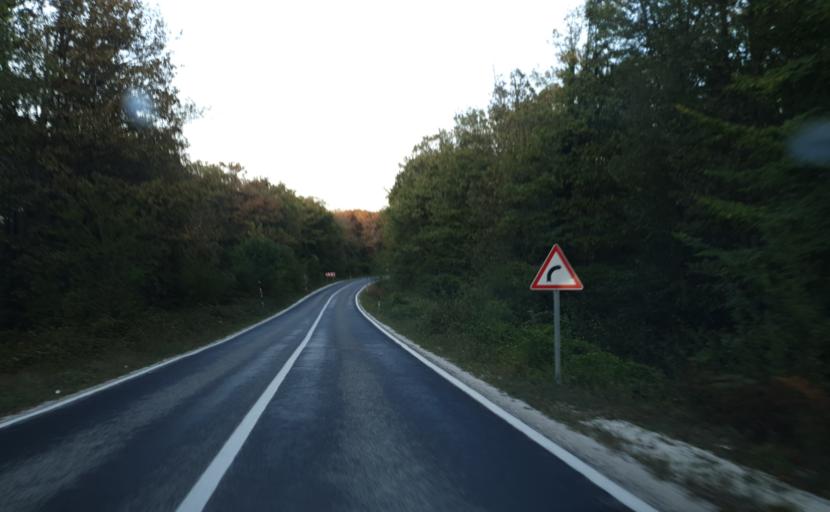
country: TR
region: Kirklareli
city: Igneada
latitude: 41.8673
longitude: 27.8419
